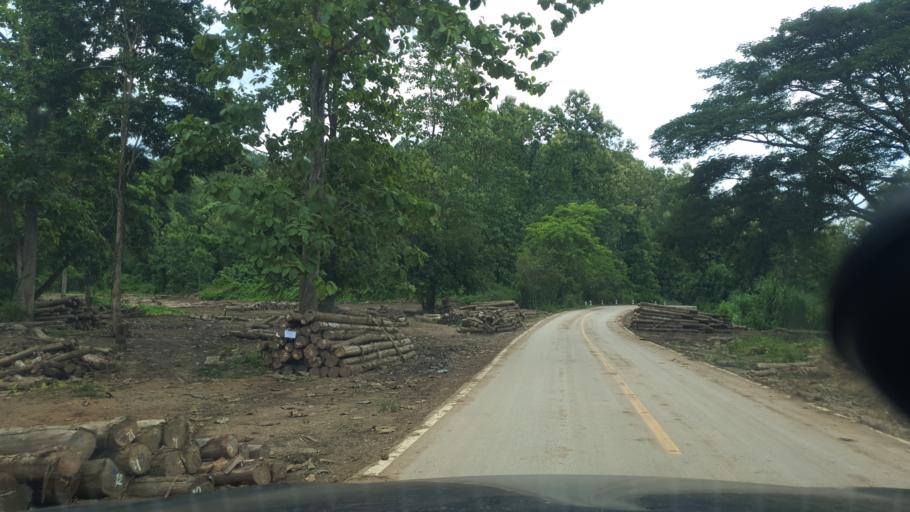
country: TH
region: Lampang
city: Hang Chat
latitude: 18.3742
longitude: 99.2596
